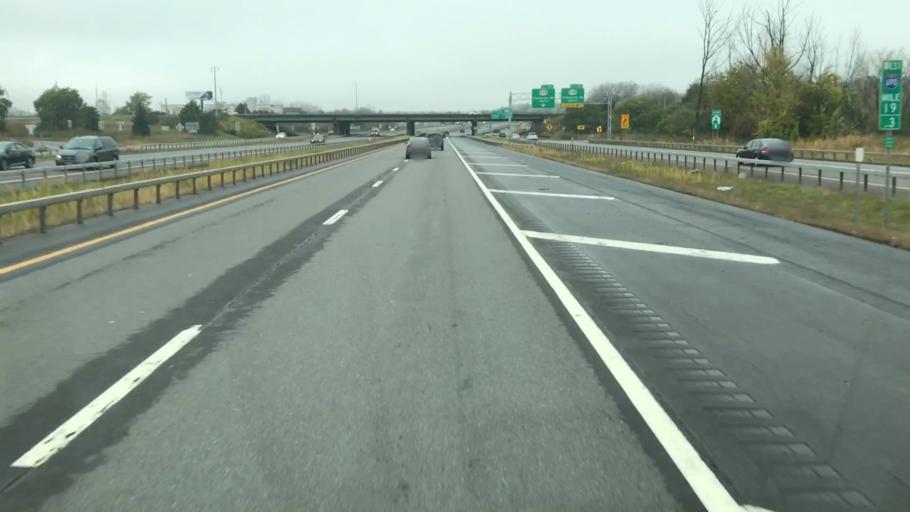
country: US
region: New York
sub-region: Onondaga County
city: East Syracuse
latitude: 43.0582
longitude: -76.0800
